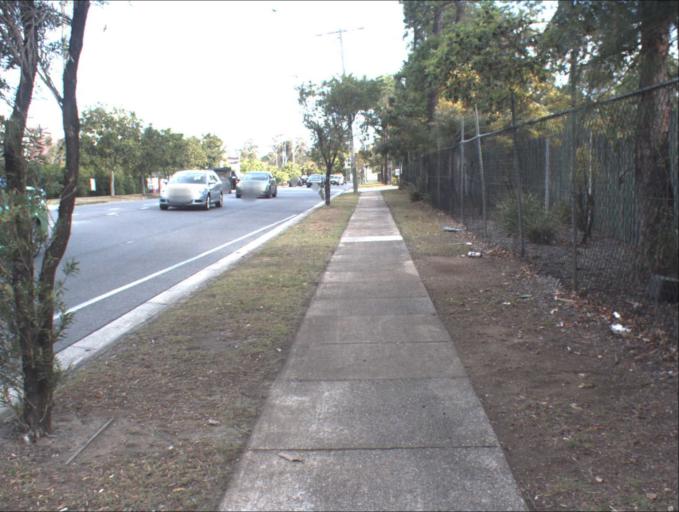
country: AU
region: Queensland
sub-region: Logan
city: Waterford West
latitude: -27.6658
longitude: 153.1237
